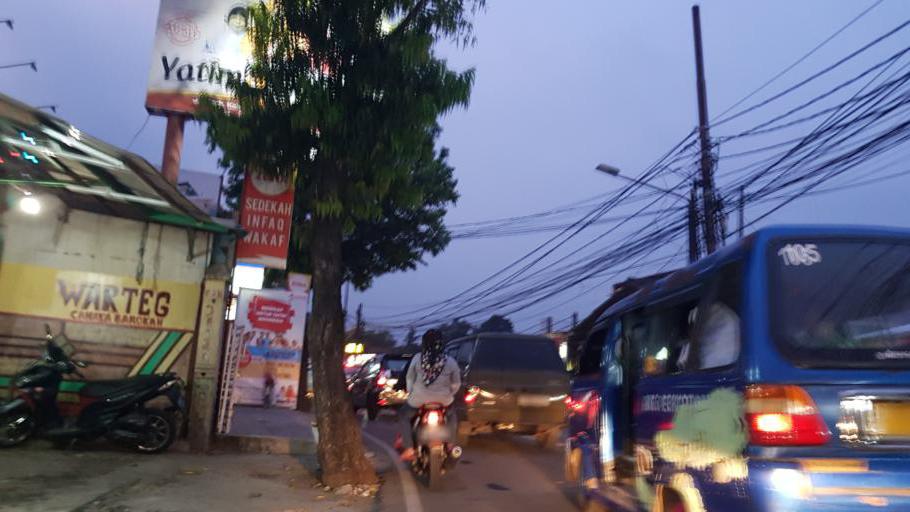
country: ID
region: West Java
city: Depok
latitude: -6.3454
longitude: 106.8037
